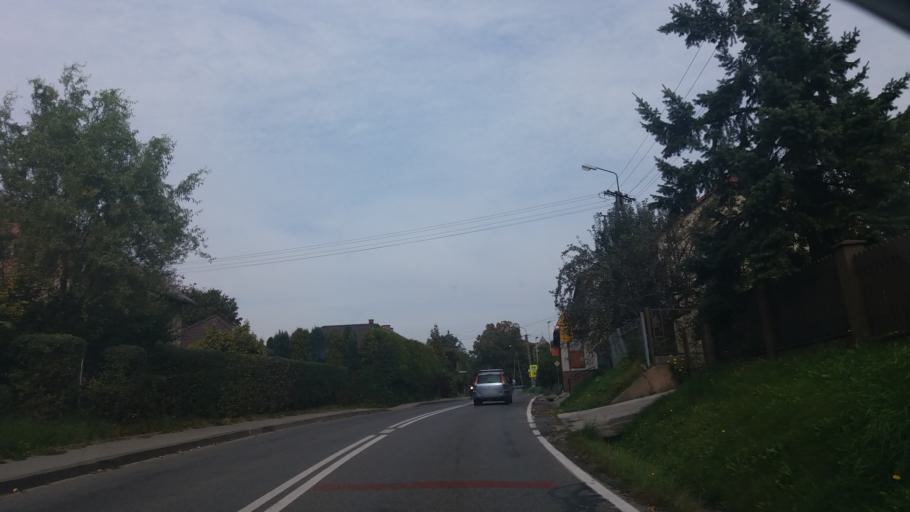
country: PL
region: Lesser Poland Voivodeship
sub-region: Powiat chrzanowski
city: Plaza
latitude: 50.0975
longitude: 19.4633
